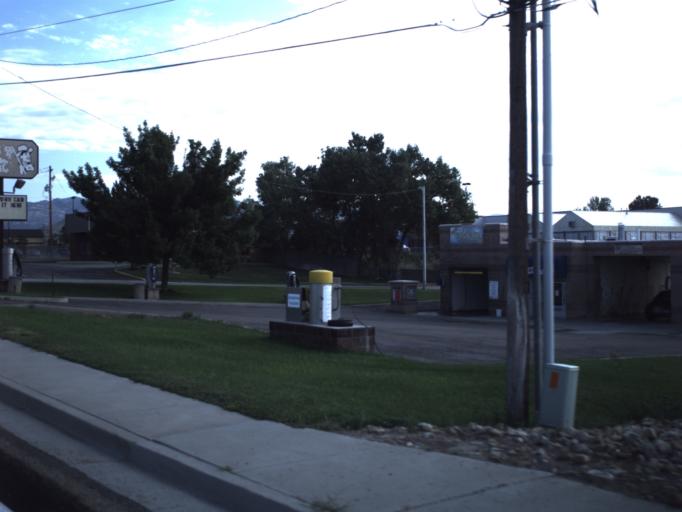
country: US
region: Utah
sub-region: Carbon County
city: Price
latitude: 39.5944
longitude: -110.7905
